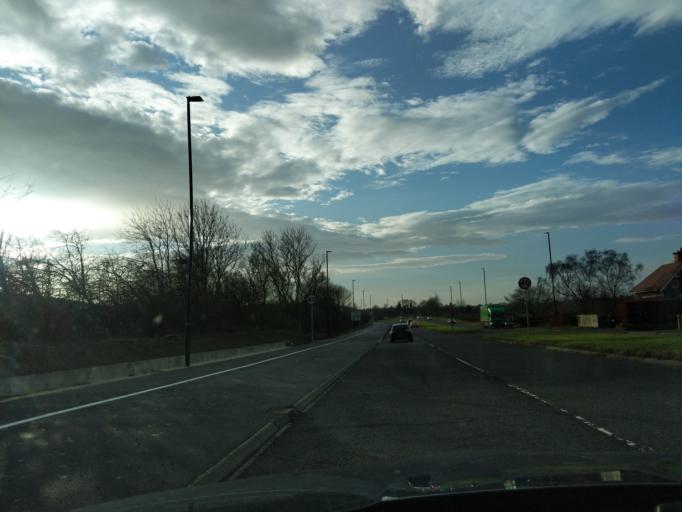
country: GB
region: England
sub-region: Newcastle upon Tyne
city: Gosforth
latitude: 55.0201
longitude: -1.5966
